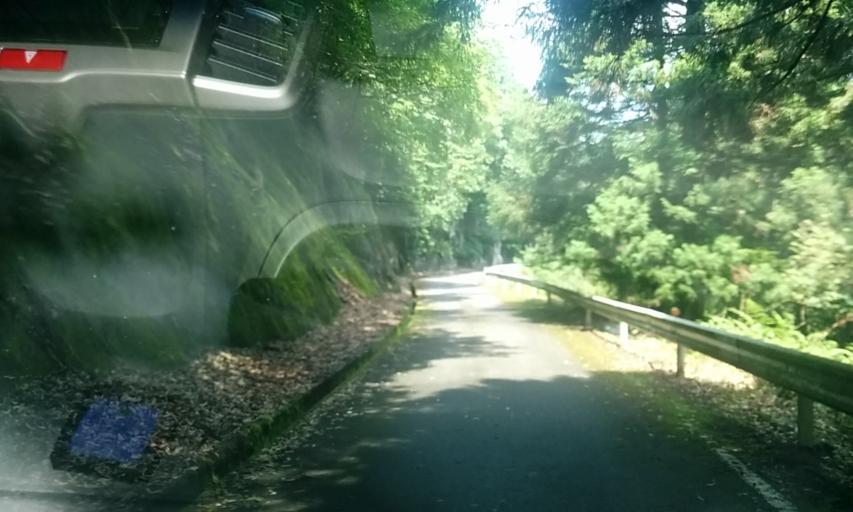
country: JP
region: Hyogo
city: Sasayama
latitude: 35.1671
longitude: 135.2009
